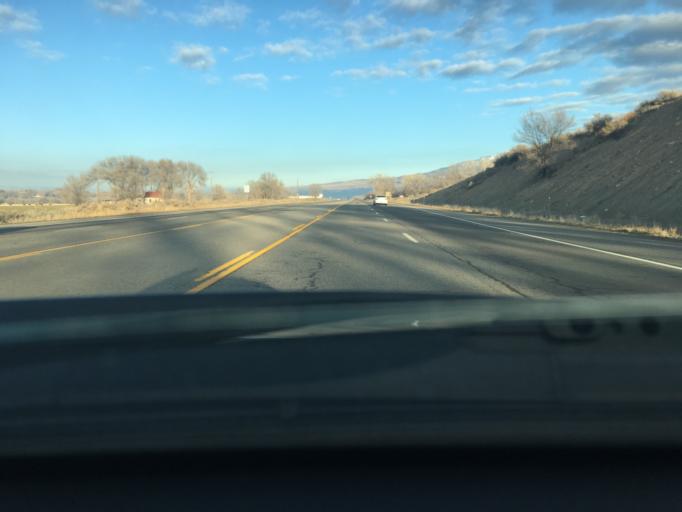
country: US
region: Colorado
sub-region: Delta County
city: Delta
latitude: 38.7125
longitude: -108.0499
